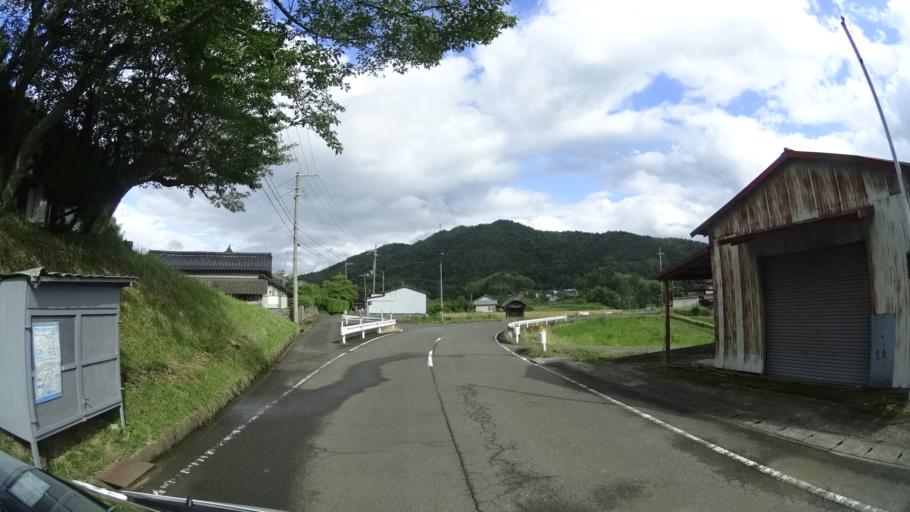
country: JP
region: Kyoto
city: Ayabe
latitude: 35.3572
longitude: 135.2927
